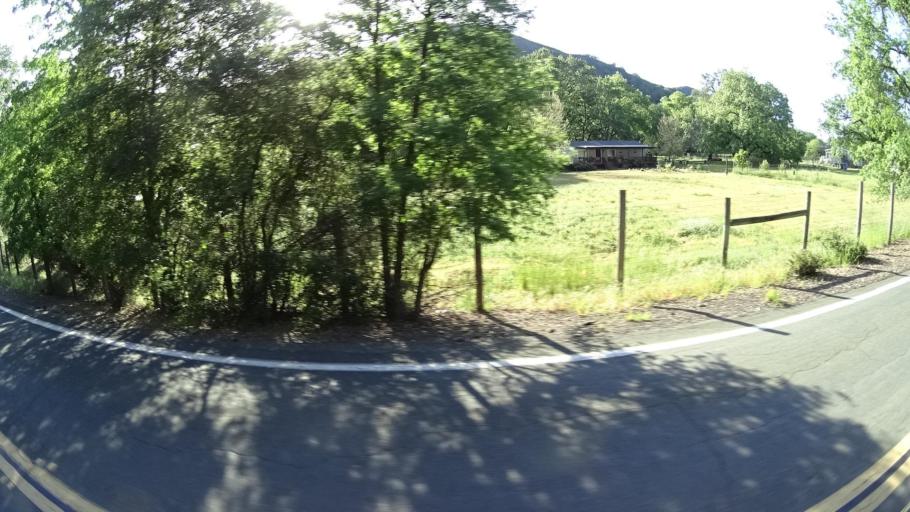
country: US
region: California
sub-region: Lake County
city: Upper Lake
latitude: 39.1353
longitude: -122.9984
